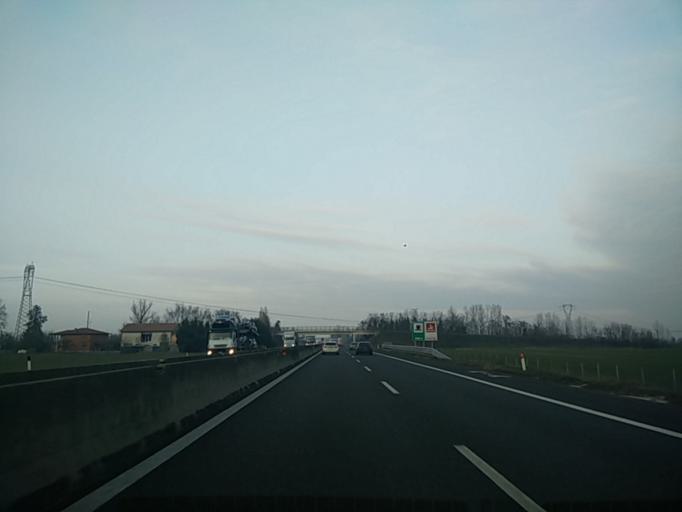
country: IT
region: Emilia-Romagna
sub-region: Provincia di Bologna
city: Bentivoglio
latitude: 44.6048
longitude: 11.4090
